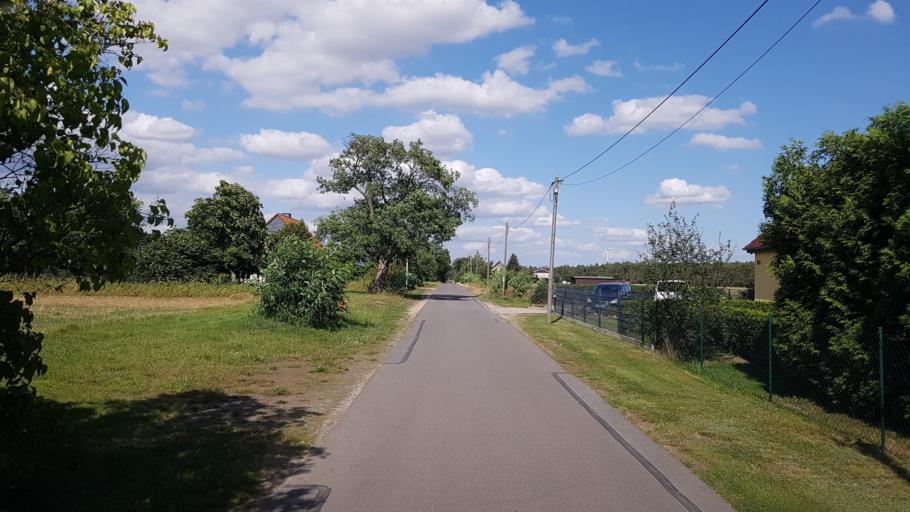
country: DE
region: Brandenburg
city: Muhlberg
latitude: 51.4479
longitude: 13.2937
